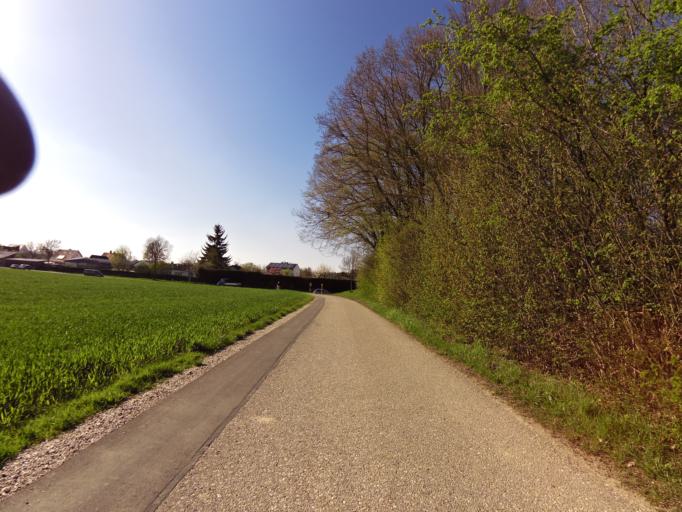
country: DE
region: Bavaria
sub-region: Lower Bavaria
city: Eching
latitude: 48.5075
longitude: 12.0791
